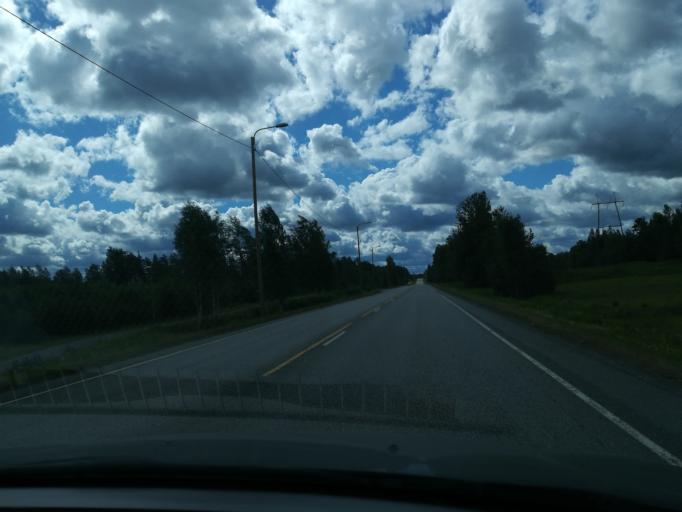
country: FI
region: Southern Savonia
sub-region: Mikkeli
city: Ristiina
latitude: 61.4894
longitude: 27.2456
